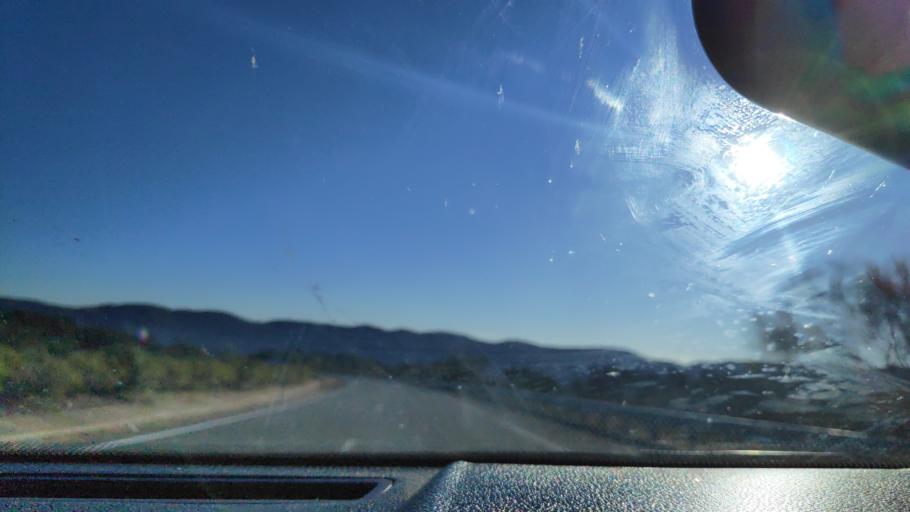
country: ES
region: Andalusia
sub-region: Provincia de Sevilla
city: El Ronquillo
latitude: 37.6944
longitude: -6.1831
